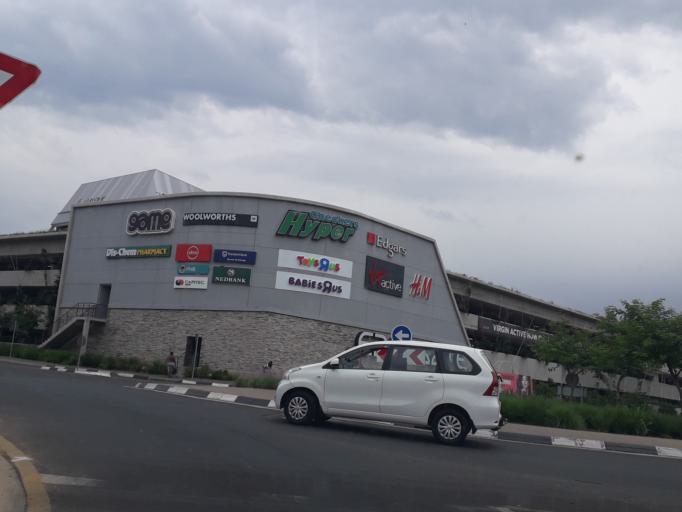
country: ZA
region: Gauteng
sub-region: City of Johannesburg Metropolitan Municipality
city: Johannesburg
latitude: -26.1773
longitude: 28.1181
